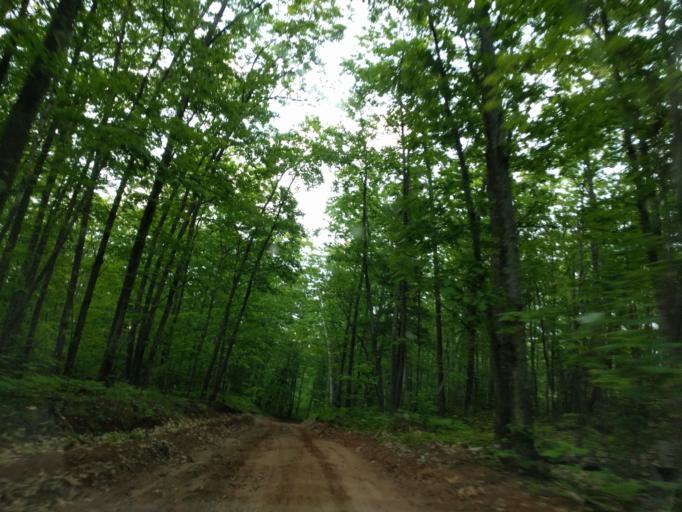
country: US
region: Michigan
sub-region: Marquette County
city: Trowbridge Park
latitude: 46.6175
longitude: -87.5000
